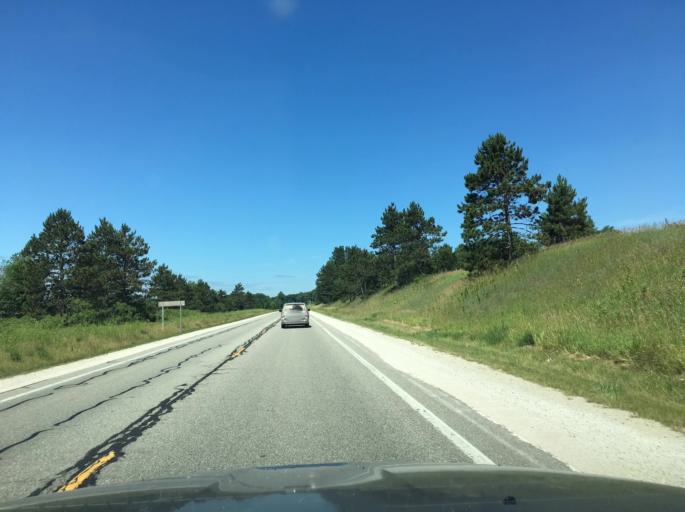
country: US
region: Michigan
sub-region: Osceola County
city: Reed City
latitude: 43.8889
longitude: -85.6442
